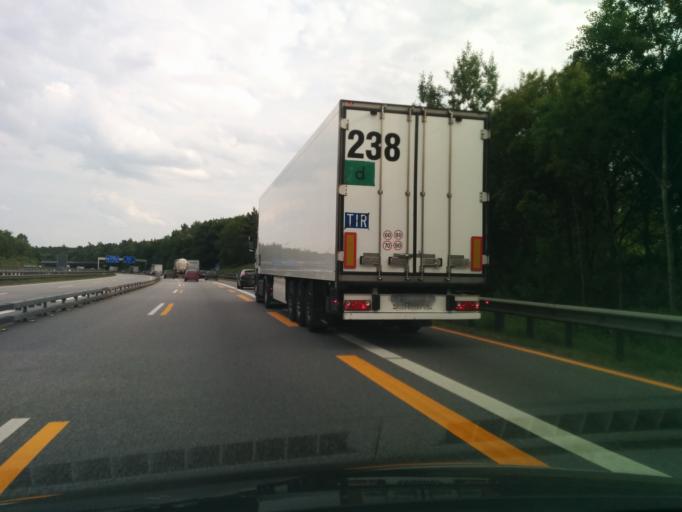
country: DE
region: Lower Saxony
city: Seevetal
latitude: 53.4433
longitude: 9.9189
